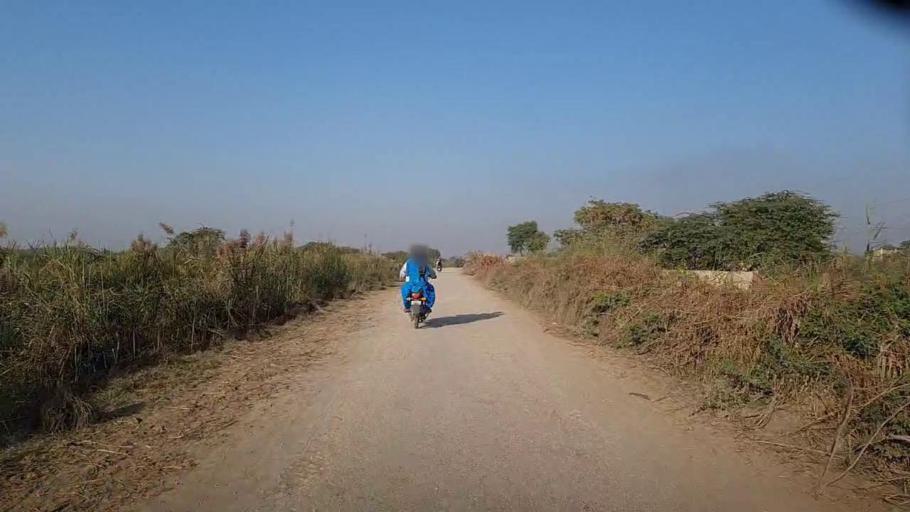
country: PK
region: Sindh
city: Ranipur
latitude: 27.2587
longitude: 68.5113
